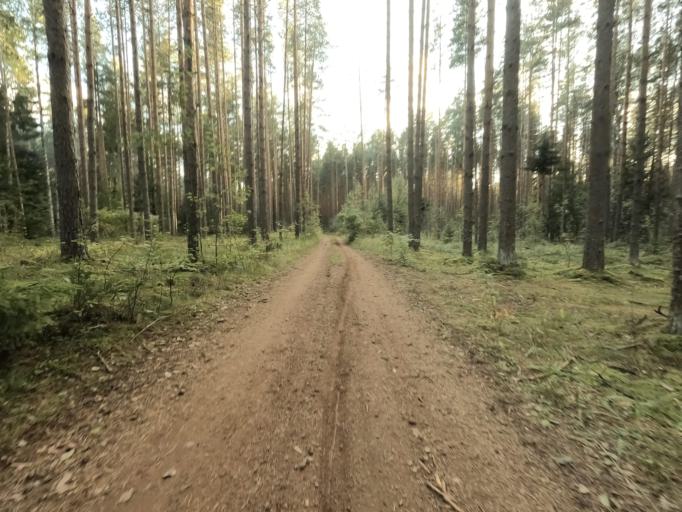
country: RU
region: Leningrad
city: Otradnoye
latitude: 59.8354
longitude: 30.7667
